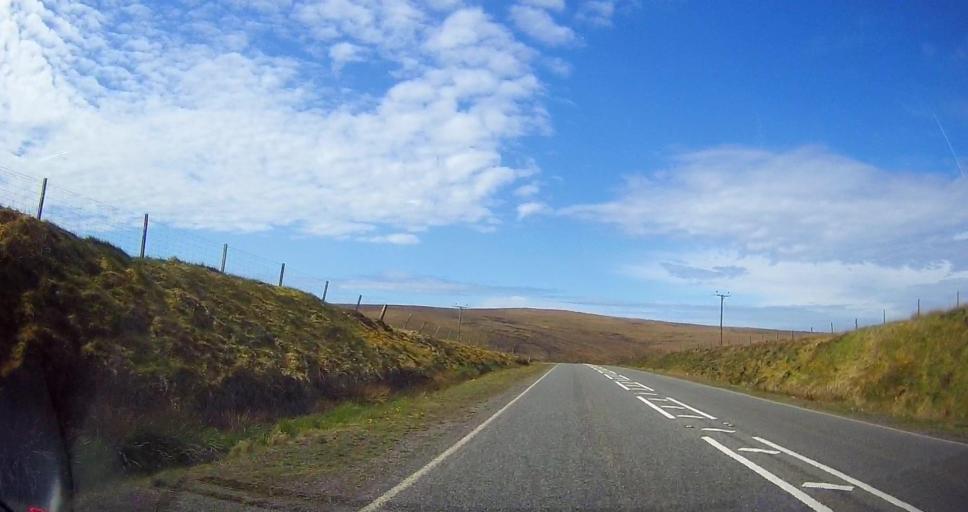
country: GB
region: Scotland
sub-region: Shetland Islands
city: Sandwick
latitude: 60.0090
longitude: -1.2674
